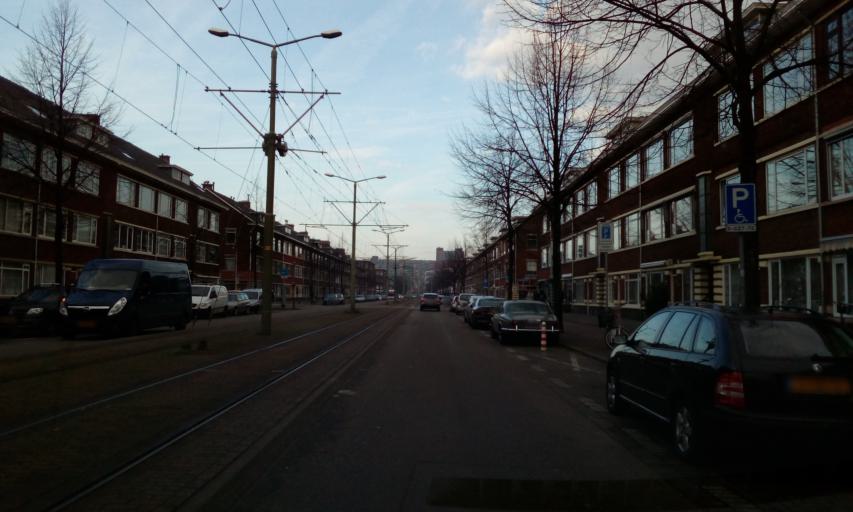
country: NL
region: South Holland
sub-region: Gemeente Rijswijk
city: Rijswijk
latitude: 52.0562
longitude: 4.3238
